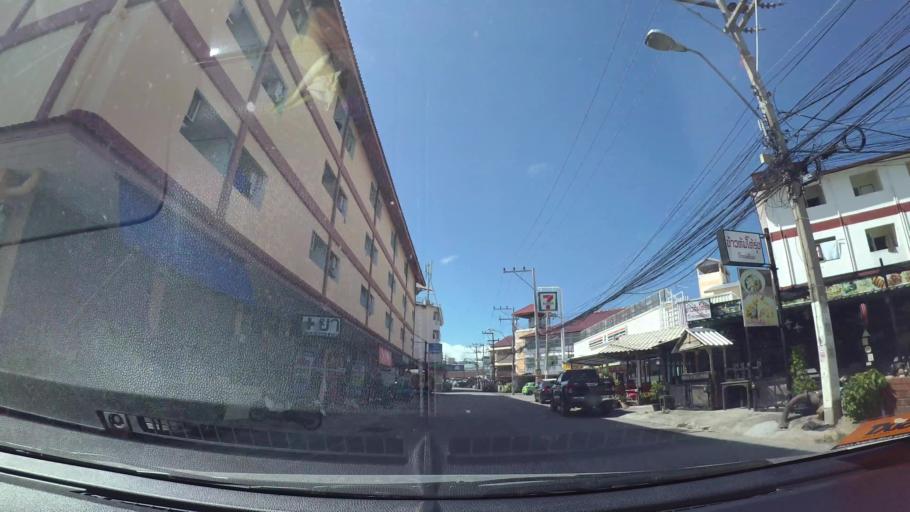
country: TH
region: Chon Buri
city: Phatthaya
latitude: 12.9302
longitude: 100.8971
